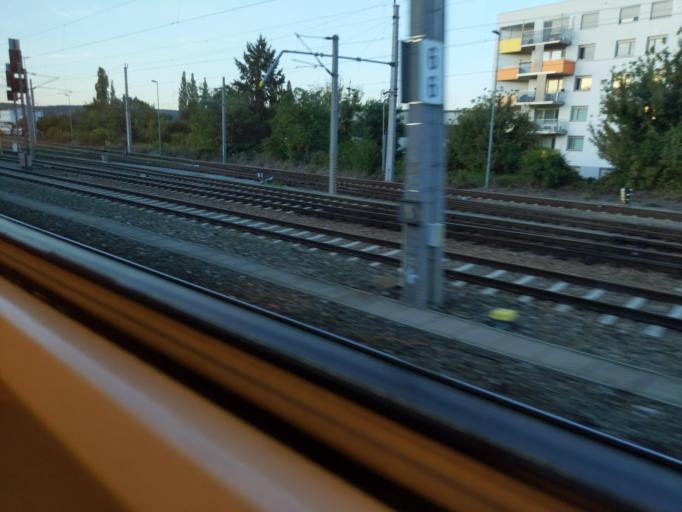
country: AT
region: Lower Austria
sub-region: Politischer Bezirk Korneuburg
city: Langenzersdorf
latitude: 48.2751
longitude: 16.3948
